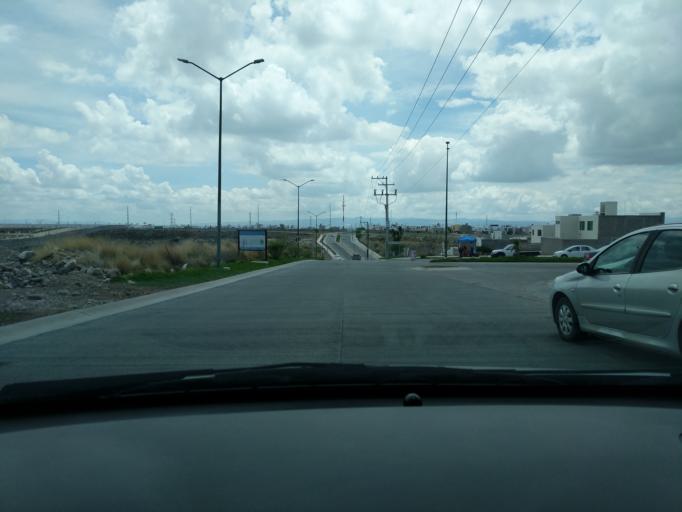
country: MX
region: San Luis Potosi
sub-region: Mexquitic de Carmona
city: Guadalupe Victoria
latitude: 22.1626
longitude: -101.0495
